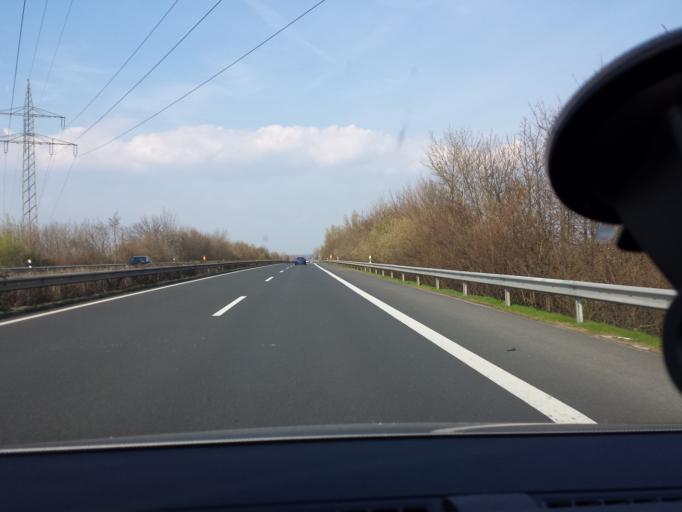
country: DE
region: Lower Saxony
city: Leiferde
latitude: 52.1660
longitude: 10.4962
